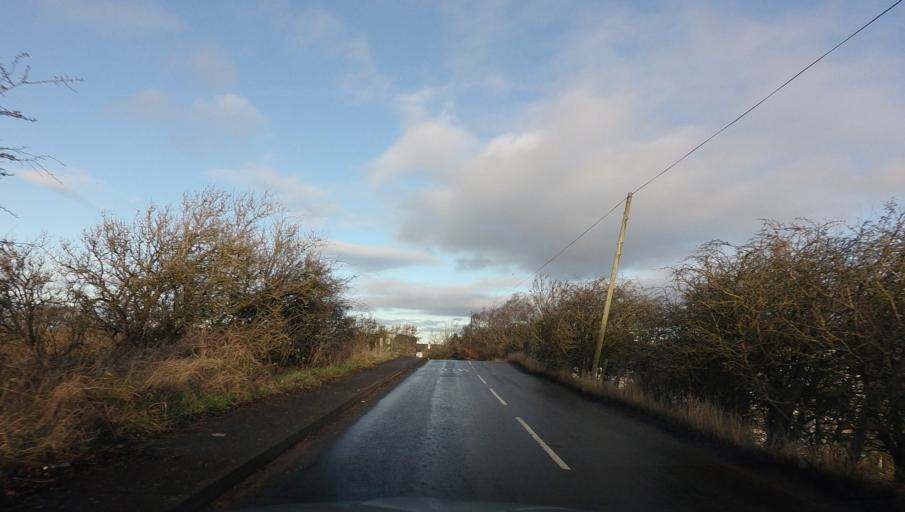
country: GB
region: Scotland
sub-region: West Lothian
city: East Calder
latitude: 55.8958
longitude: -3.4429
